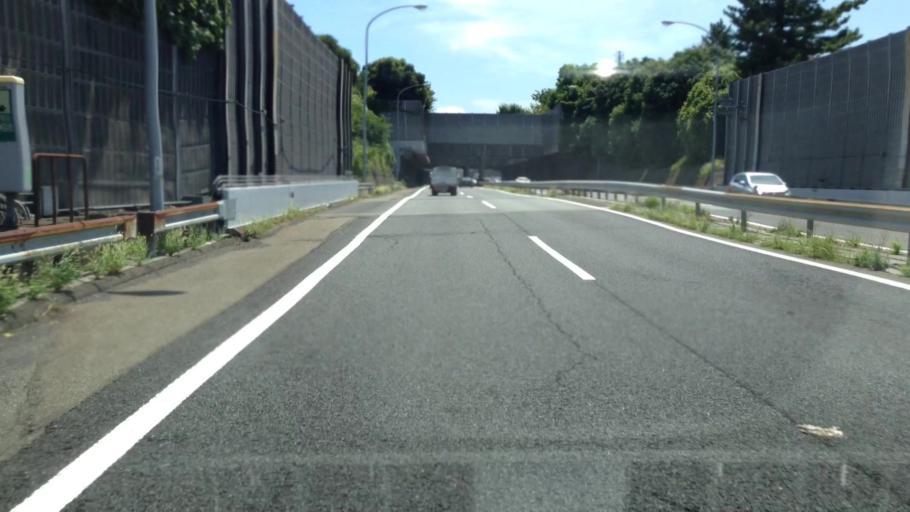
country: JP
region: Kanagawa
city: Yokohama
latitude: 35.4057
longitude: 139.5753
